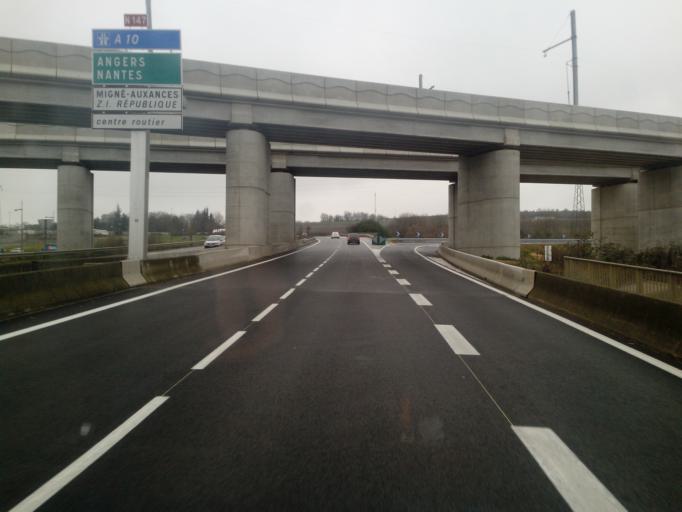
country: FR
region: Poitou-Charentes
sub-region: Departement de la Vienne
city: Chasseneuil-du-Poitou
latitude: 46.6195
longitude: 0.3535
